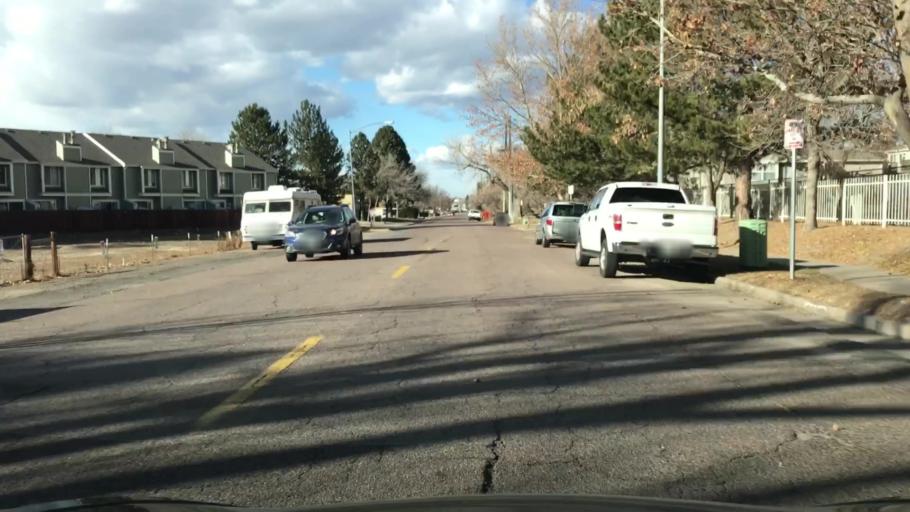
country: US
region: Colorado
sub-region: Arapahoe County
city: Glendale
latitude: 39.6909
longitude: -104.8981
